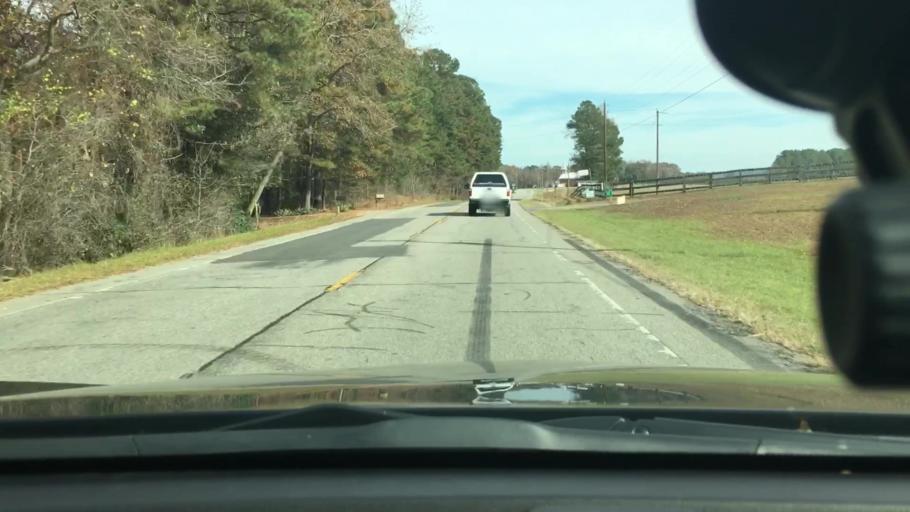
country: US
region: North Carolina
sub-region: Moore County
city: Carthage
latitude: 35.3798
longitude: -79.2844
